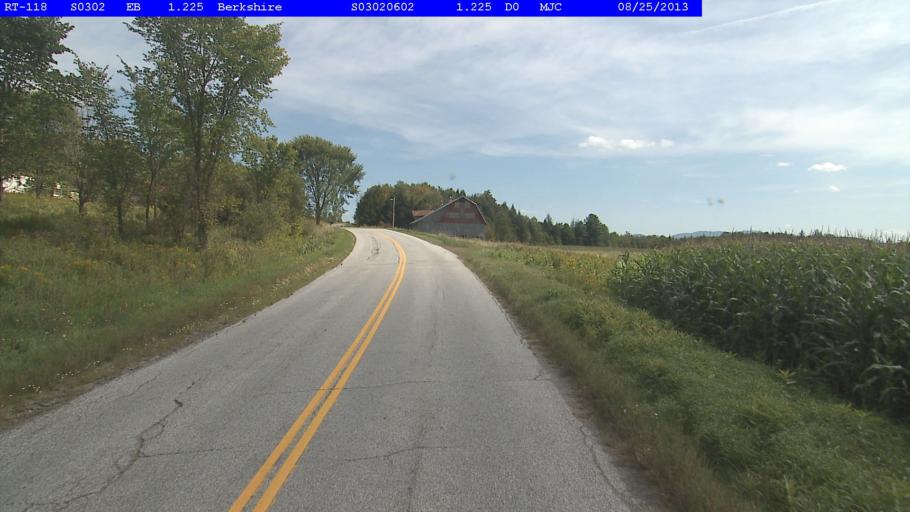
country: US
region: Vermont
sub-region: Franklin County
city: Enosburg Falls
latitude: 44.9817
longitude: -72.7919
